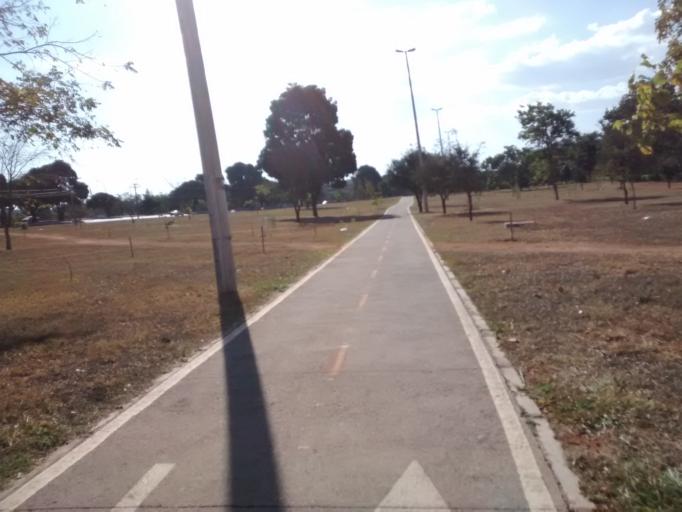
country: BR
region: Federal District
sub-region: Brasilia
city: Brasilia
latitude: -15.8006
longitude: -47.9318
